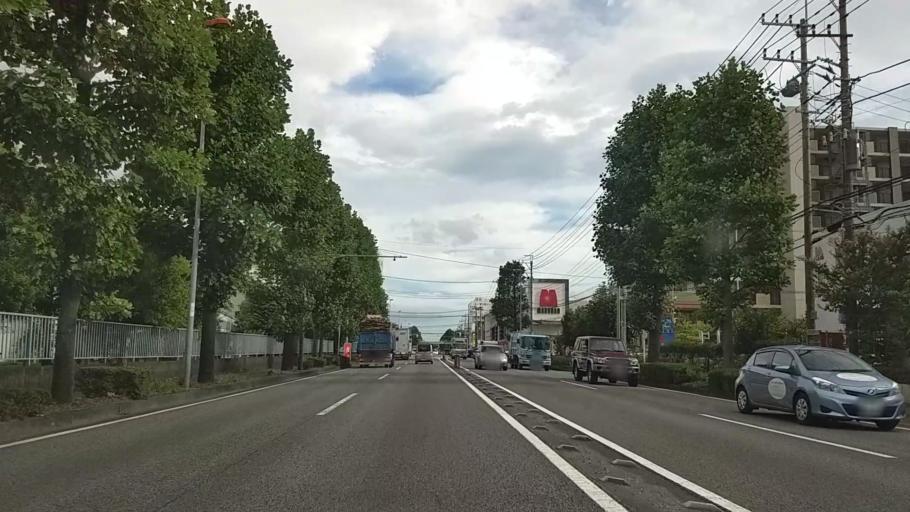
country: JP
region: Tokyo
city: Hachioji
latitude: 35.5823
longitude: 139.3461
